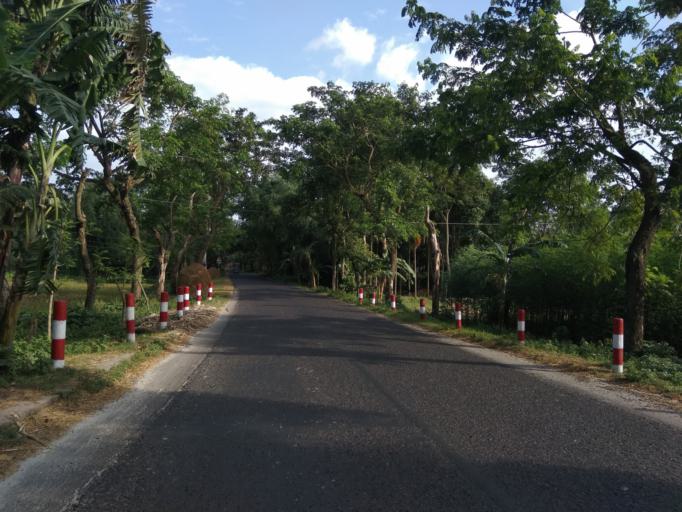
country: BD
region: Rangpur Division
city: Rangpur
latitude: 25.8392
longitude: 89.1138
